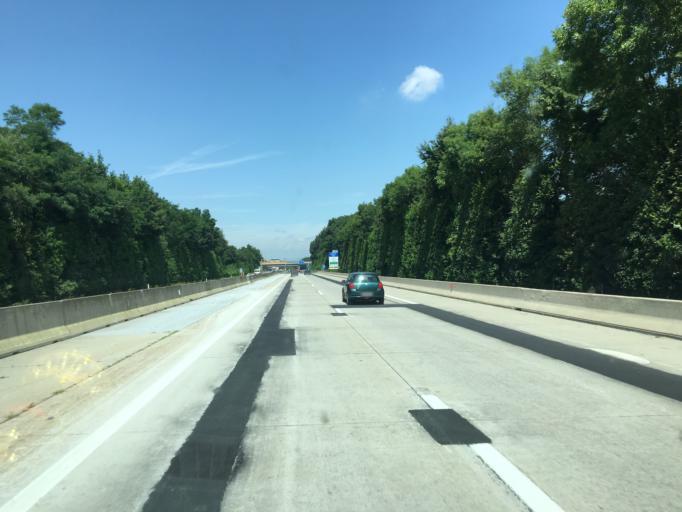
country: AT
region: Styria
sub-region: Politischer Bezirk Leibnitz
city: Gabersdorf
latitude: 46.8007
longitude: 15.5706
